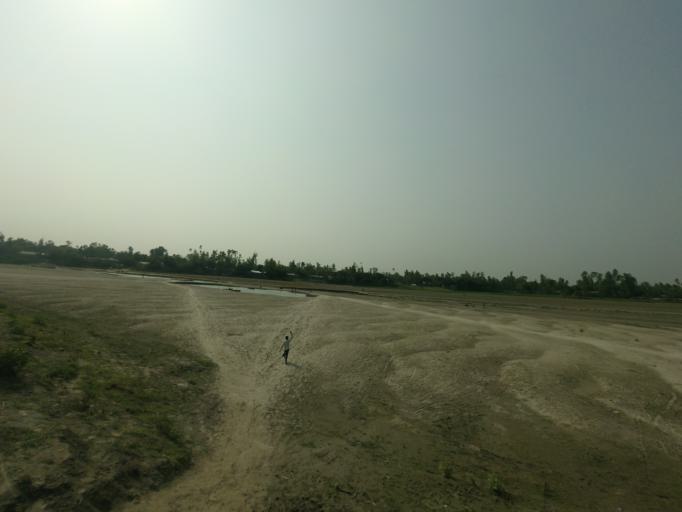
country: BD
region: Rajshahi
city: Sirajganj
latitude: 24.3335
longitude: 89.7176
